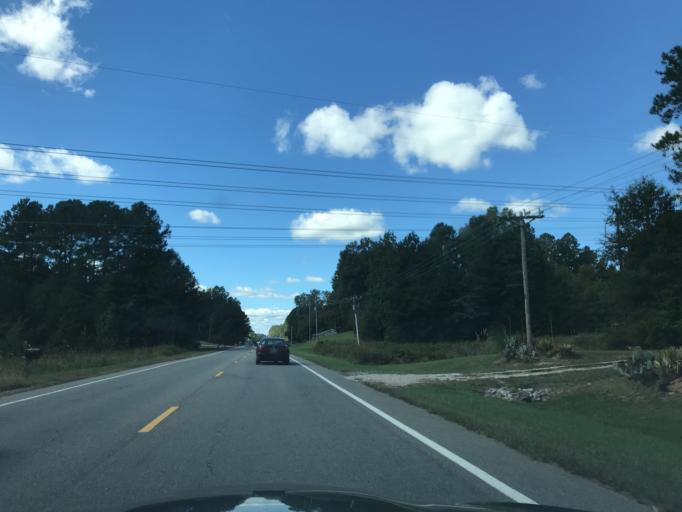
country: US
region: North Carolina
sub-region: Durham County
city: Gorman
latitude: 35.9788
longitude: -78.7645
